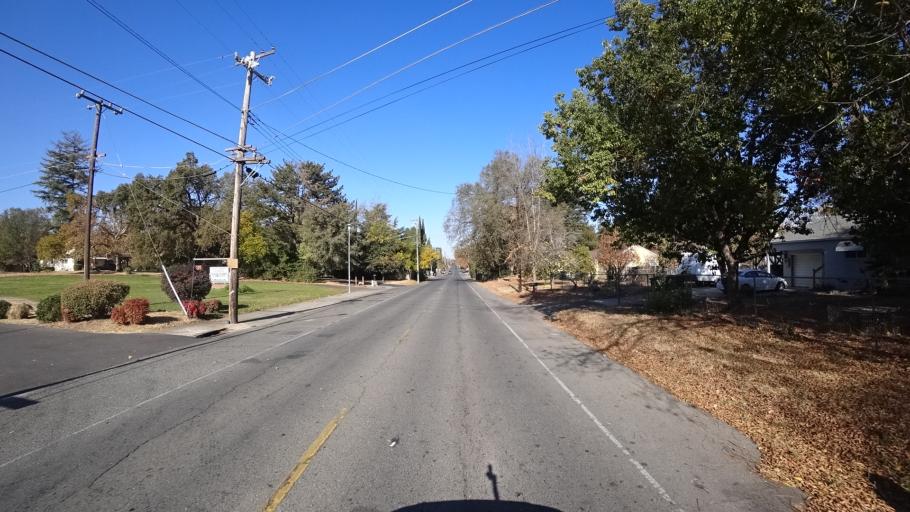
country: US
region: California
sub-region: Sacramento County
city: Citrus Heights
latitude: 38.7007
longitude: -121.2811
